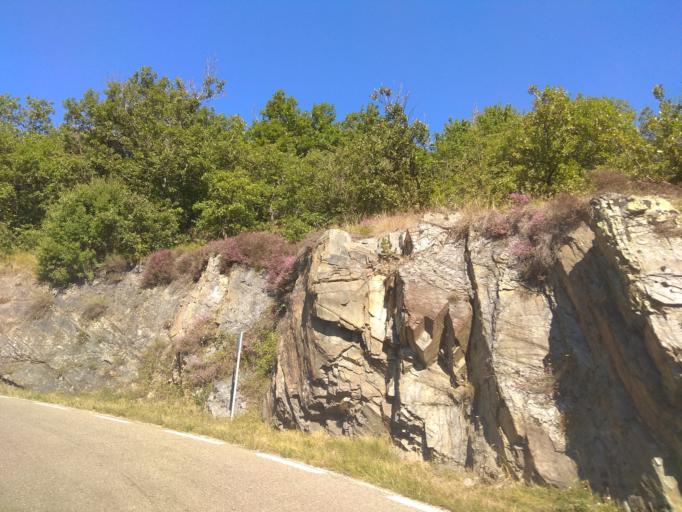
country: ES
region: Catalonia
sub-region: Provincia de Lleida
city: Vielha
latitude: 42.7441
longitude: 0.7441
